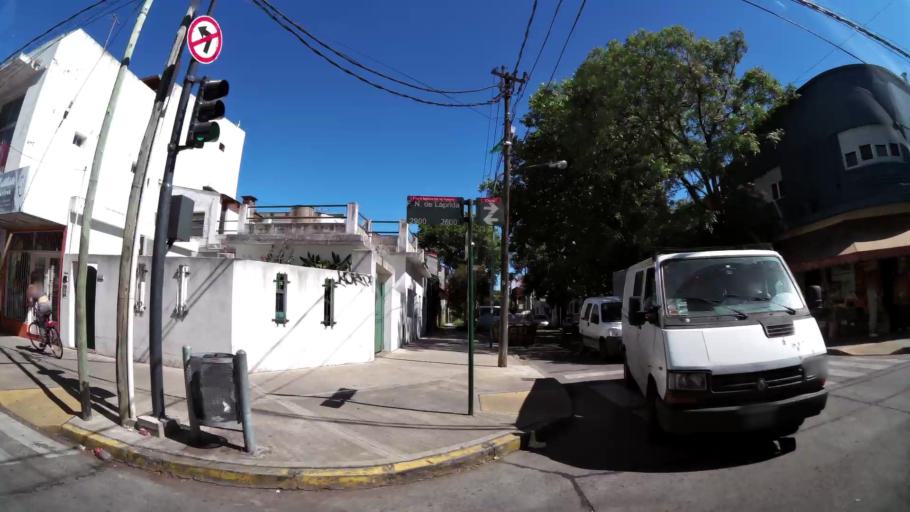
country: AR
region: Buenos Aires
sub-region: Partido de Vicente Lopez
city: Olivos
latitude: -34.5428
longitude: -58.4933
